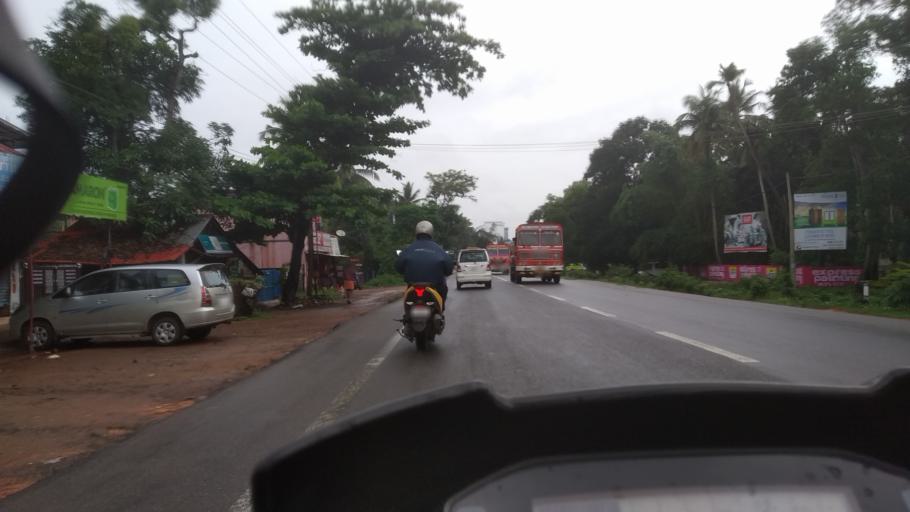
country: IN
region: Kerala
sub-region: Alappuzha
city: Kayankulam
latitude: 9.1276
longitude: 76.5161
